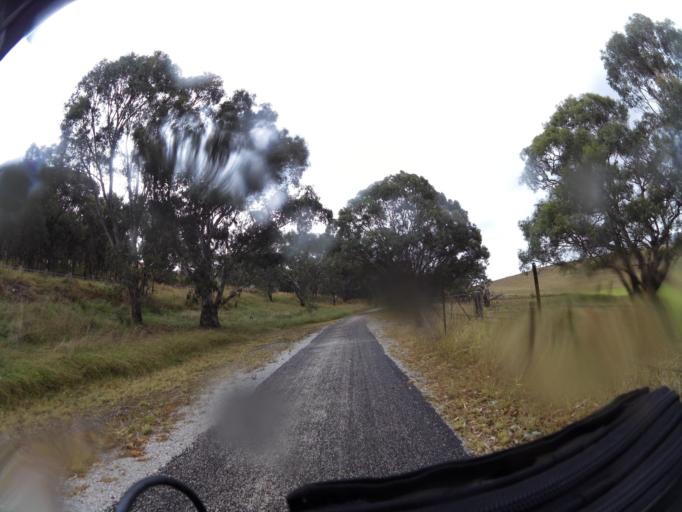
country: AU
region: New South Wales
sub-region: Albury Municipality
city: East Albury
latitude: -36.2162
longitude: 147.2362
